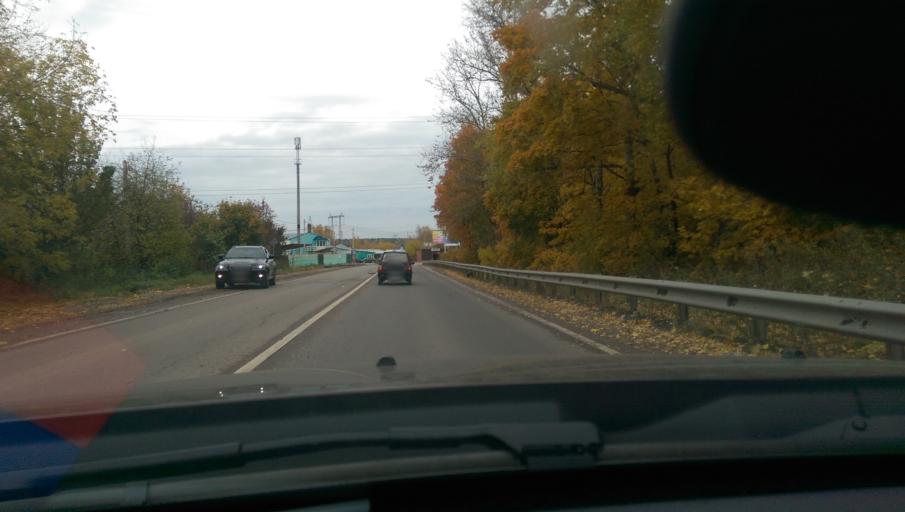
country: RU
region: Moskovskaya
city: Pirogovskiy
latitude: 55.9709
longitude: 37.7148
